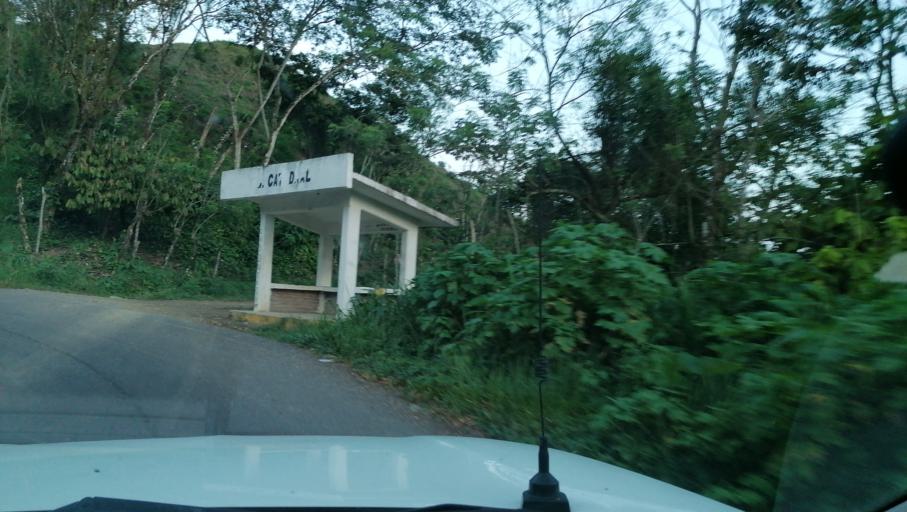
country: MX
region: Chiapas
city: Ostuacan
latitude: 17.4229
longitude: -93.3372
